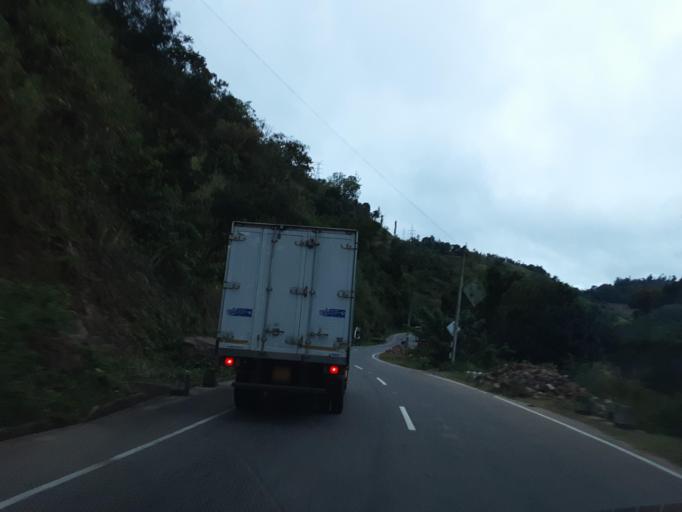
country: LK
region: Uva
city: Badulla
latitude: 6.9137
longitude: 80.9499
